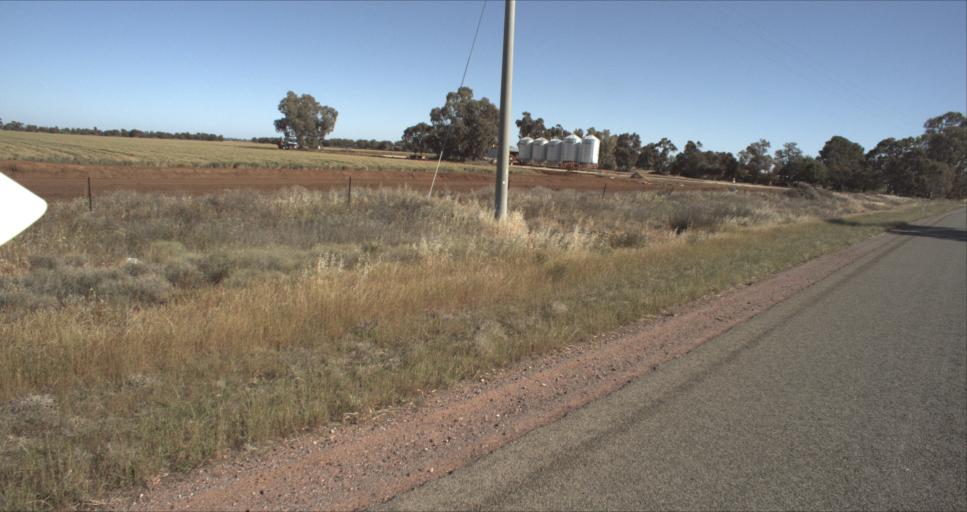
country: AU
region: New South Wales
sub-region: Leeton
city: Leeton
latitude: -34.5570
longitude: 146.2662
